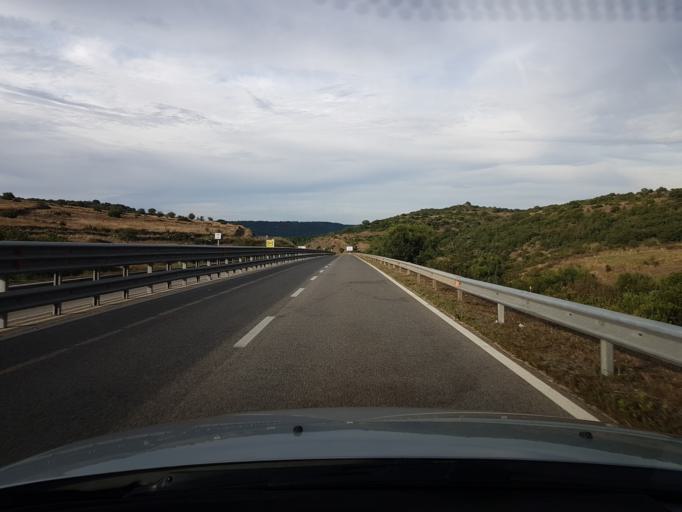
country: IT
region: Sardinia
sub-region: Provincia di Oristano
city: Soddi
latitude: 40.1327
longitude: 8.8649
